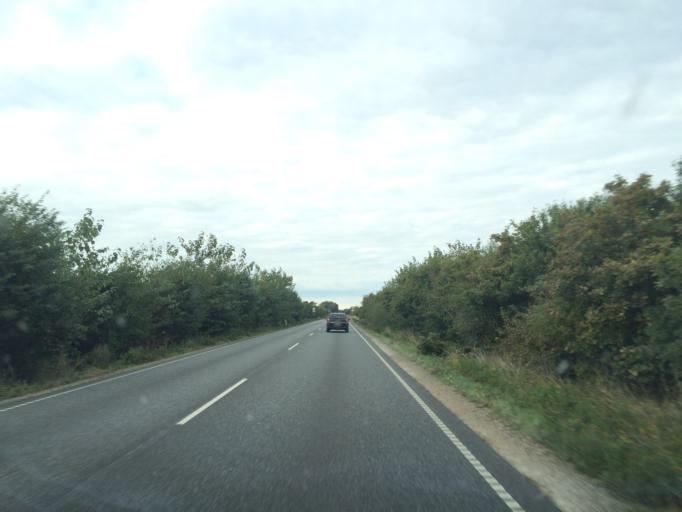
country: DK
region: Central Jutland
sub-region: Ringkobing-Skjern Kommune
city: Ringkobing
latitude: 56.1672
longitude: 8.2868
